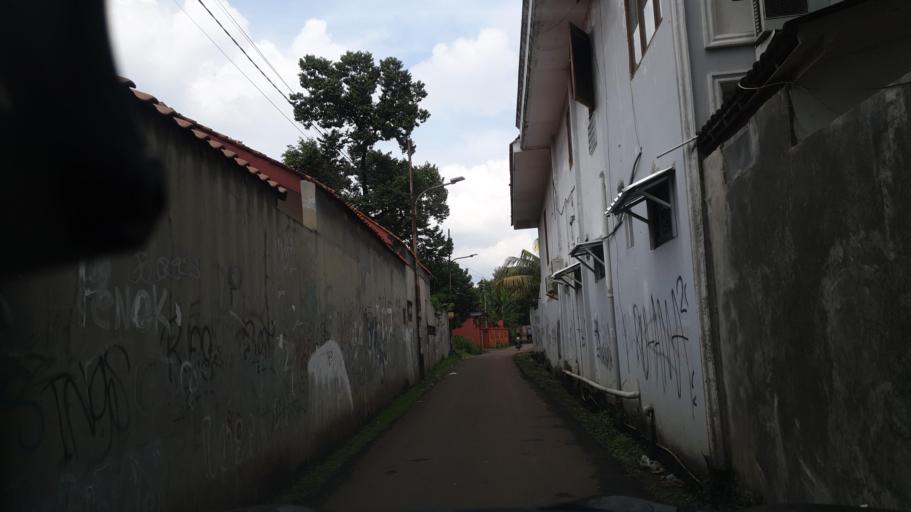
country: ID
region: West Java
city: Pamulang
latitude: -6.3371
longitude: 106.7728
